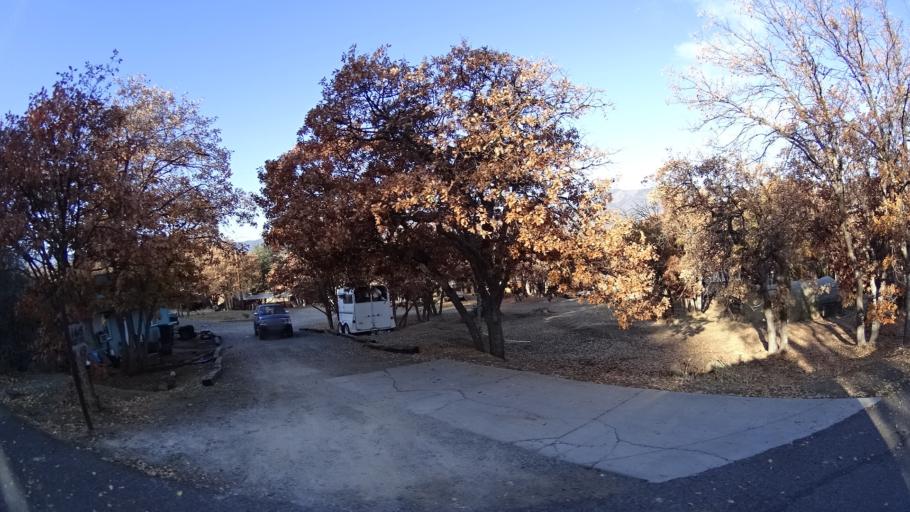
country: US
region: California
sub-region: Siskiyou County
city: Yreka
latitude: 41.7108
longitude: -122.6159
